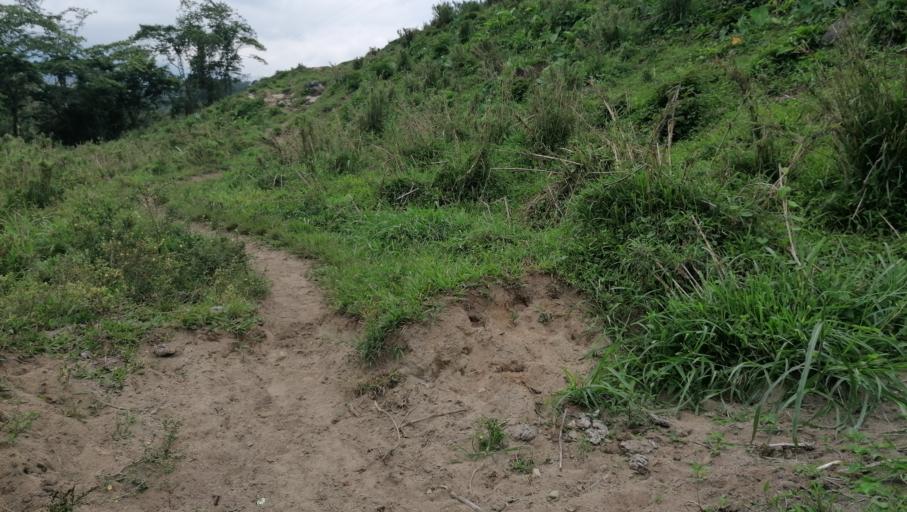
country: MX
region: Chiapas
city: Ocotepec
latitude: 17.2994
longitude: -93.2268
